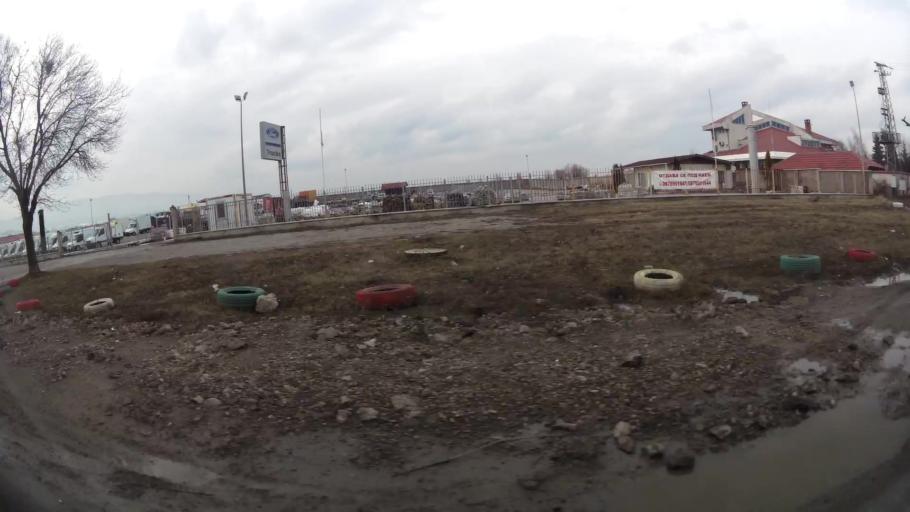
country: BG
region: Sofiya
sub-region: Obshtina Bozhurishte
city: Bozhurishte
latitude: 42.7055
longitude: 23.2303
